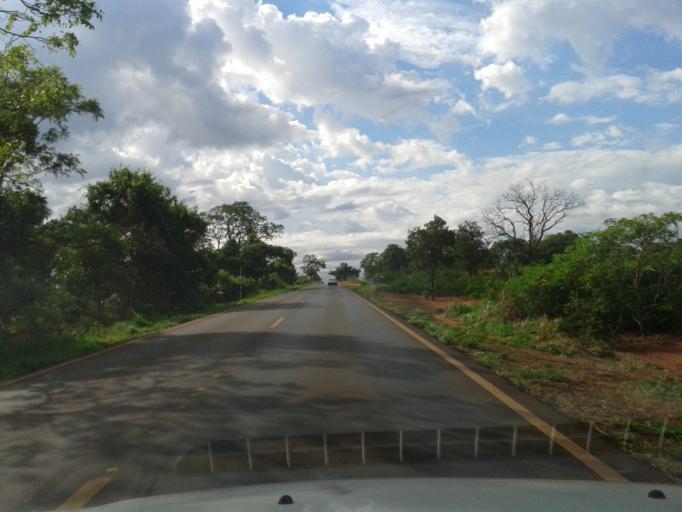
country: BR
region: Minas Gerais
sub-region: Ituiutaba
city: Ituiutaba
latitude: -18.9993
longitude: -49.7880
